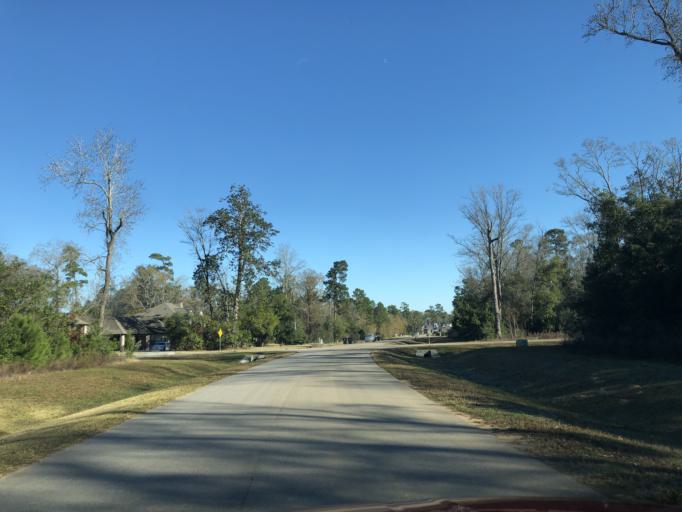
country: US
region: Texas
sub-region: Montgomery County
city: Porter Heights
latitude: 30.0729
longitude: -95.3348
